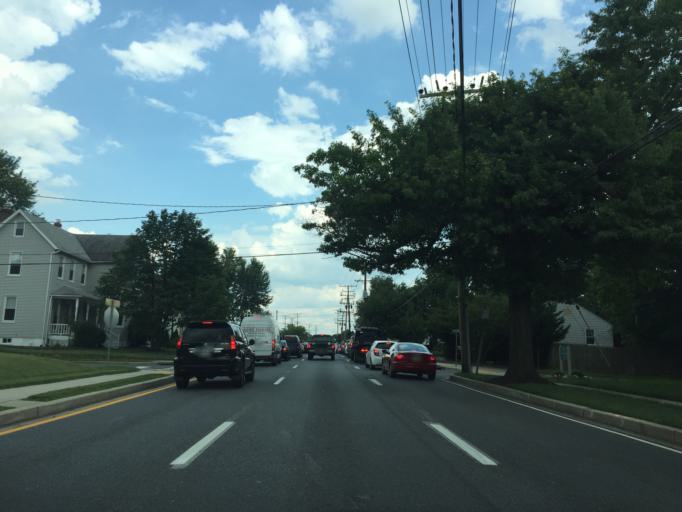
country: US
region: Maryland
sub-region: Prince George's County
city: Laurel
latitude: 39.0996
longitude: -76.8520
